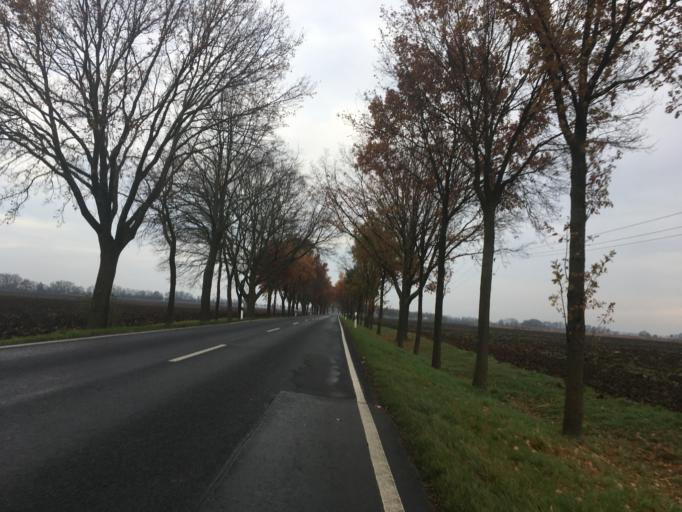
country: DE
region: Brandenburg
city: Letschin
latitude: 52.5879
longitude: 14.3427
